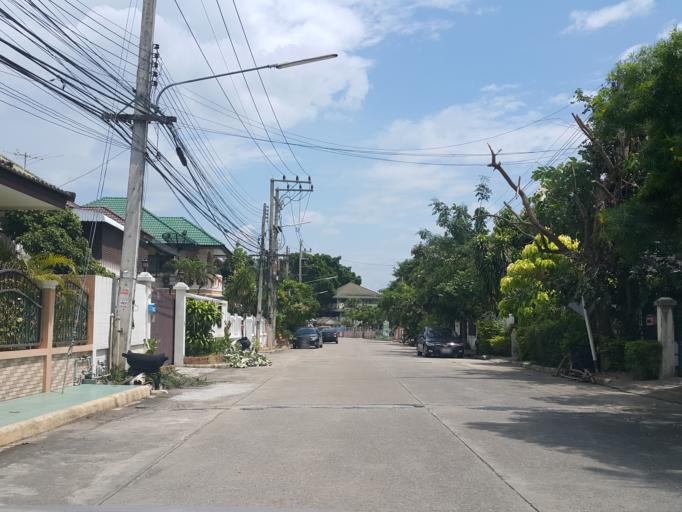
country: TH
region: Chiang Mai
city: Hang Dong
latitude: 18.7374
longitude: 98.9480
